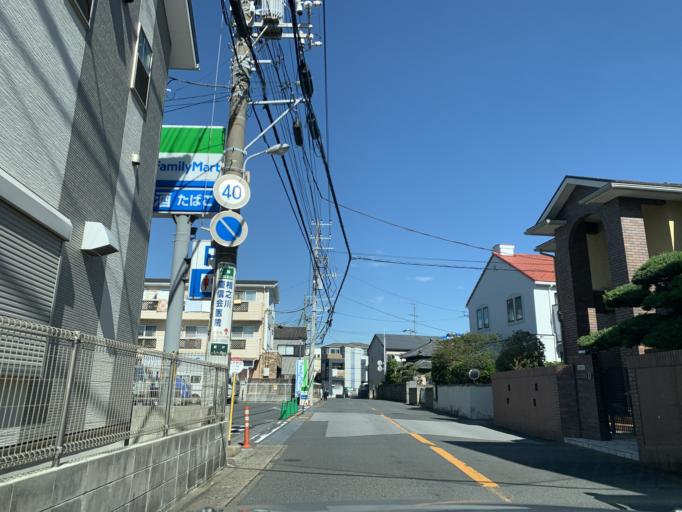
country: JP
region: Tokyo
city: Urayasu
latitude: 35.6764
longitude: 139.8927
